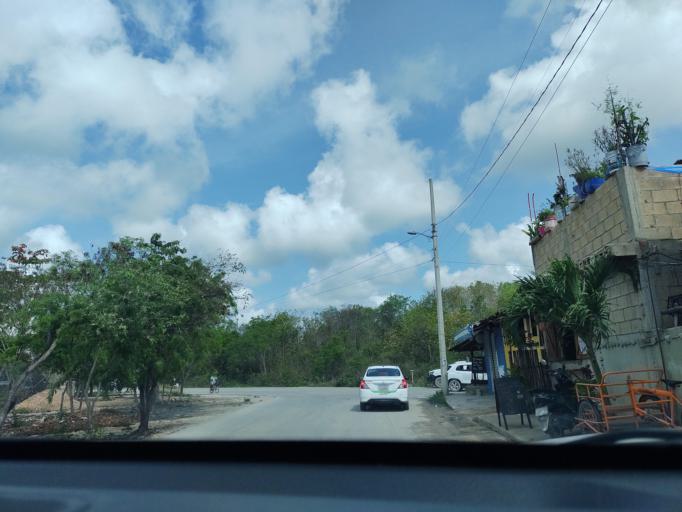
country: MX
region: Quintana Roo
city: Tulum
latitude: 20.2109
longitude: -87.4736
